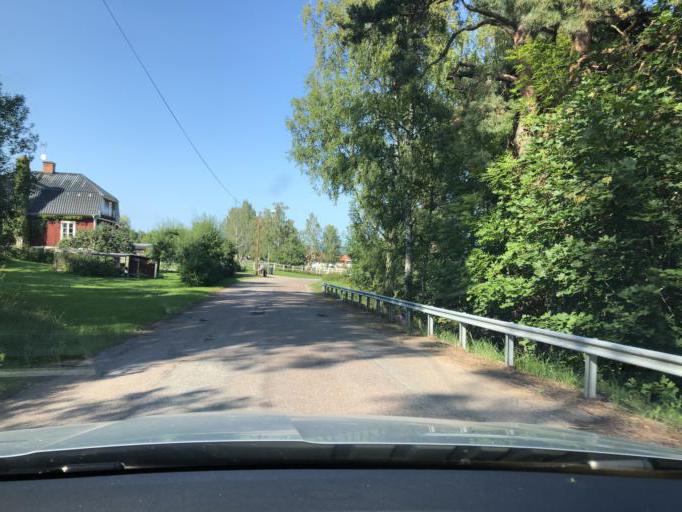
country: SE
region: Dalarna
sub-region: Hedemora Kommun
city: Hedemora
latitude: 60.3645
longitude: 15.9252
